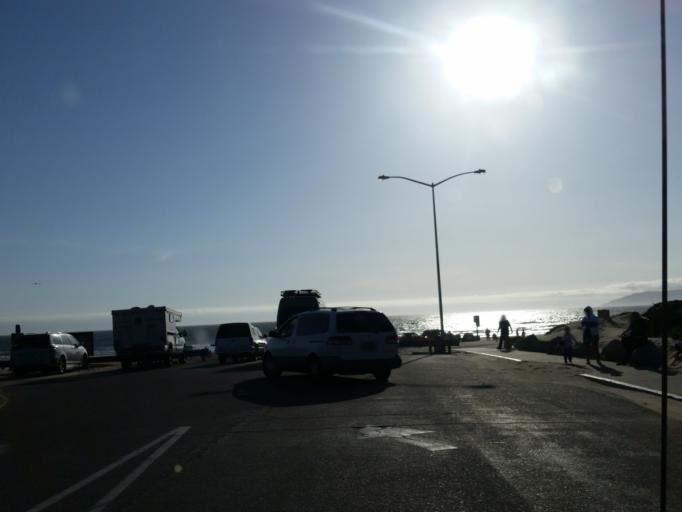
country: US
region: California
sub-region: San Luis Obispo County
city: Grover Beach
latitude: 35.1223
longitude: -120.6342
